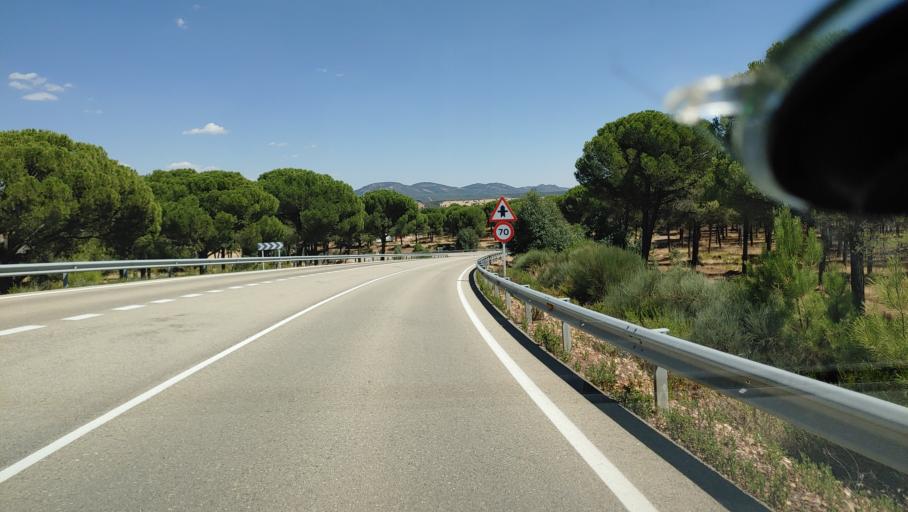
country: ES
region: Castille-La Mancha
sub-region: Provincia de Ciudad Real
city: Saceruela
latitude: 39.0096
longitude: -4.5031
